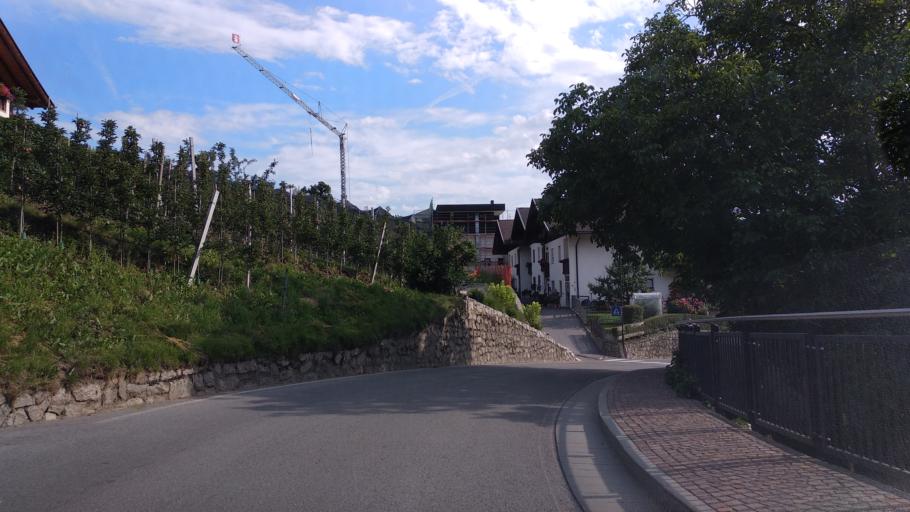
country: IT
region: Trentino-Alto Adige
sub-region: Bolzano
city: Scena
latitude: 46.6924
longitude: 11.1902
